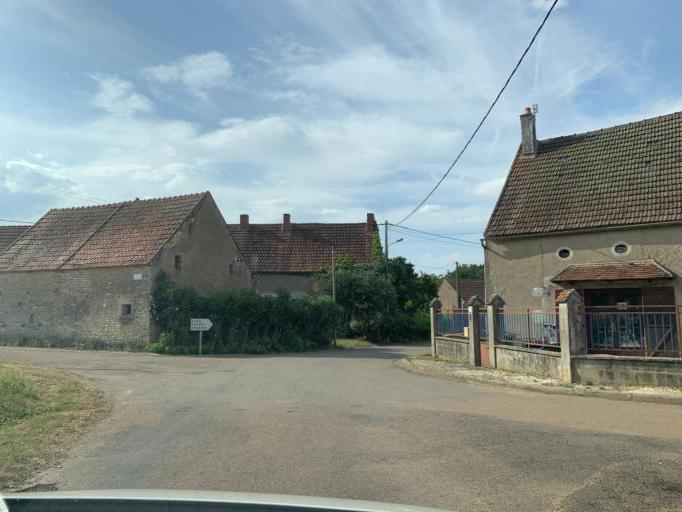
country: FR
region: Bourgogne
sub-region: Departement de l'Yonne
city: Fontenailles
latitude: 47.5172
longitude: 3.4280
